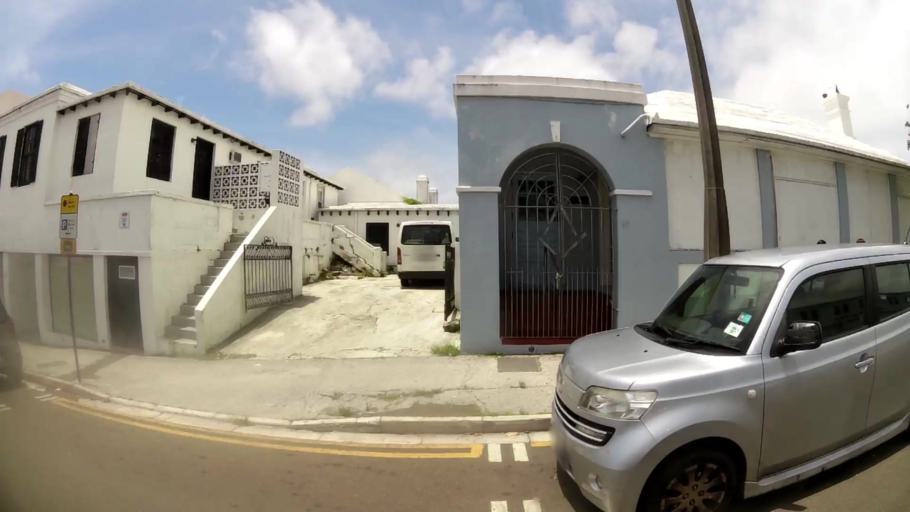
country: BM
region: Hamilton city
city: Hamilton
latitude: 32.2940
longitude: -64.7789
